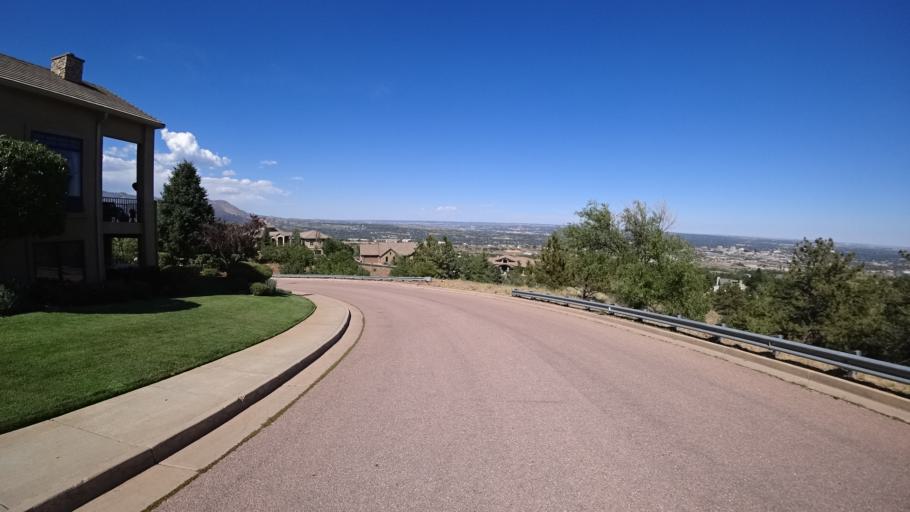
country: US
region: Colorado
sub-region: El Paso County
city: Colorado Springs
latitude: 38.8162
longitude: -104.8750
